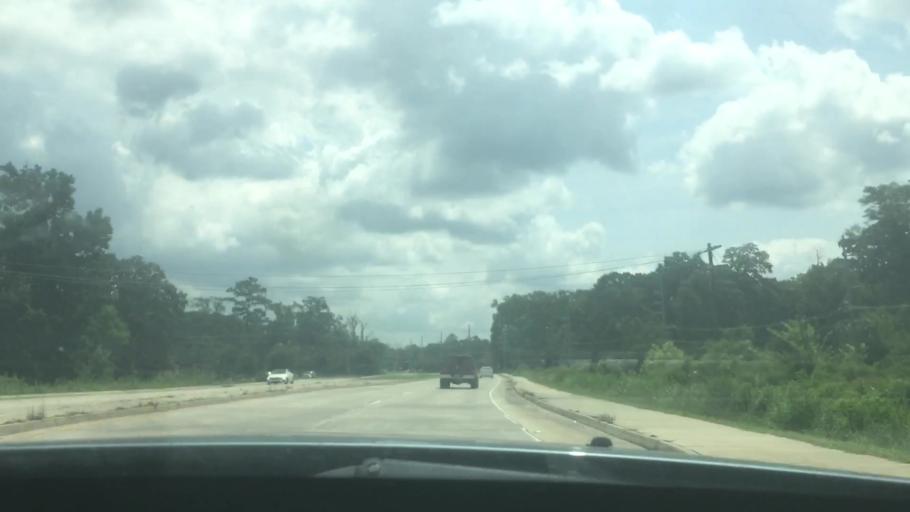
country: US
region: Louisiana
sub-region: East Baton Rouge Parish
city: Shenandoah
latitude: 30.4235
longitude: -91.0138
